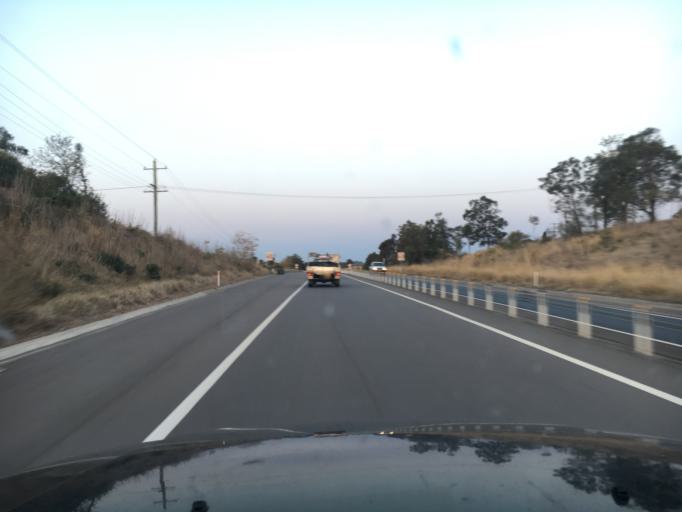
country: AU
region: New South Wales
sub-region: Cessnock
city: Greta
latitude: -32.7048
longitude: 151.4351
